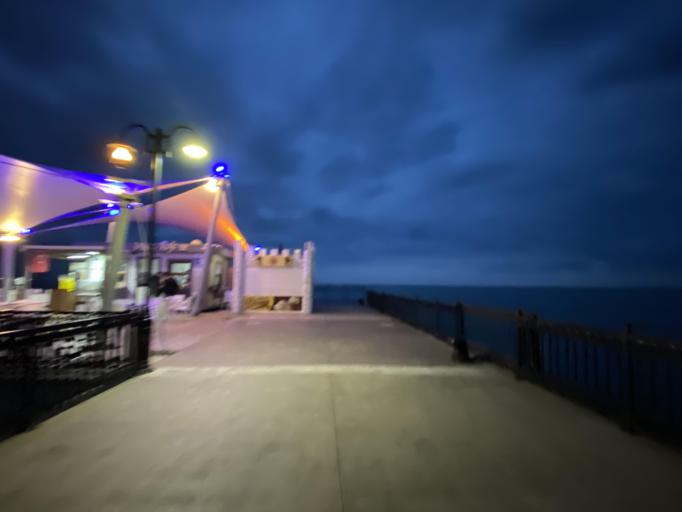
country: TR
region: Samsun
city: Samsun
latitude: 41.3462
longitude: 36.2619
